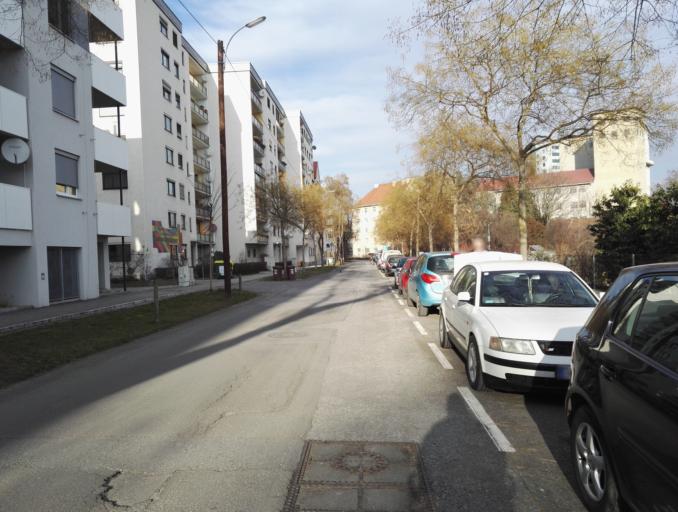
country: AT
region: Styria
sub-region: Graz Stadt
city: Graz
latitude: 47.0639
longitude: 15.4266
